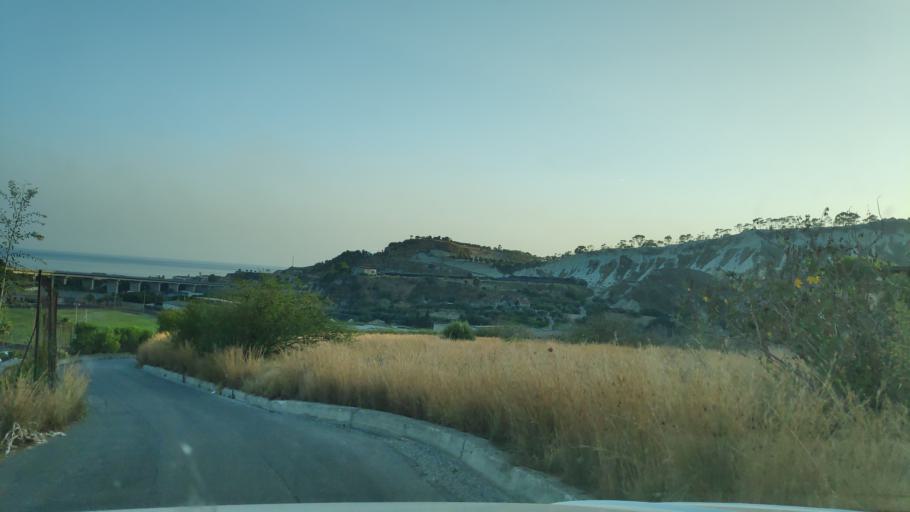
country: IT
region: Calabria
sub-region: Provincia di Reggio Calabria
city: Bova Marina
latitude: 37.9384
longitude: 15.9124
